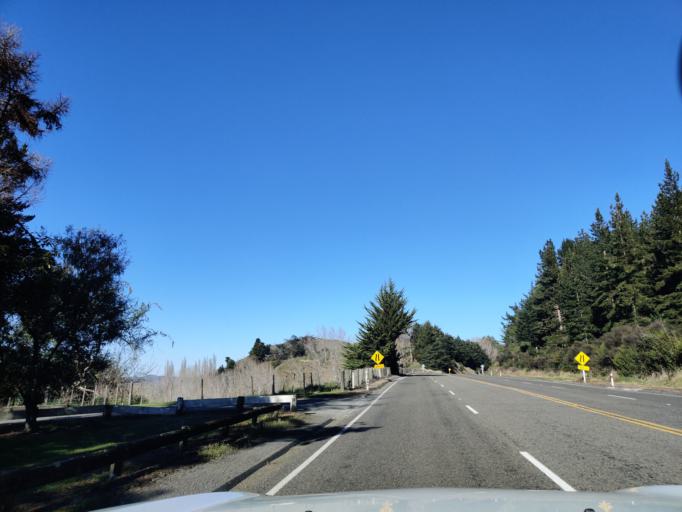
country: NZ
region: Manawatu-Wanganui
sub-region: Ruapehu District
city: Waiouru
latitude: -39.7678
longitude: 175.8000
